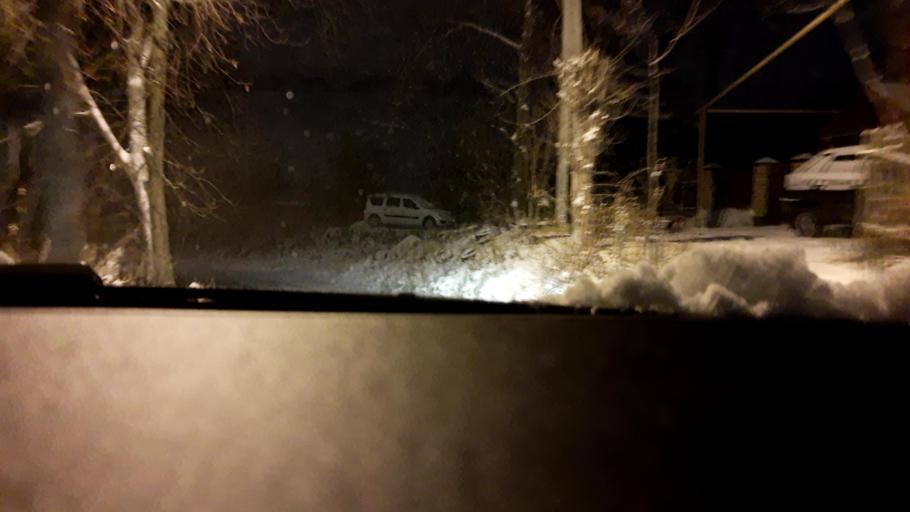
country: RU
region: Nizjnij Novgorod
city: Afonino
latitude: 56.2298
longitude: 44.0623
